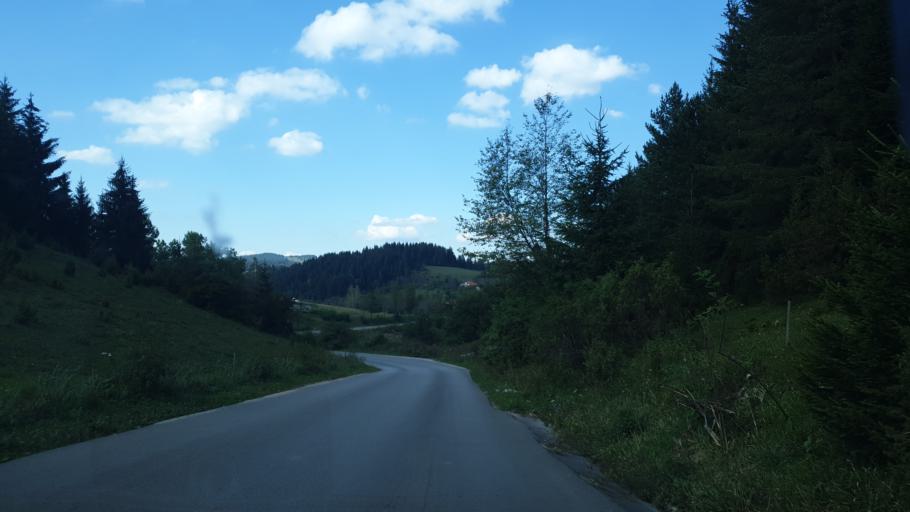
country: RS
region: Central Serbia
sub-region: Zlatiborski Okrug
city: Nova Varos
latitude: 43.4304
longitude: 19.8733
